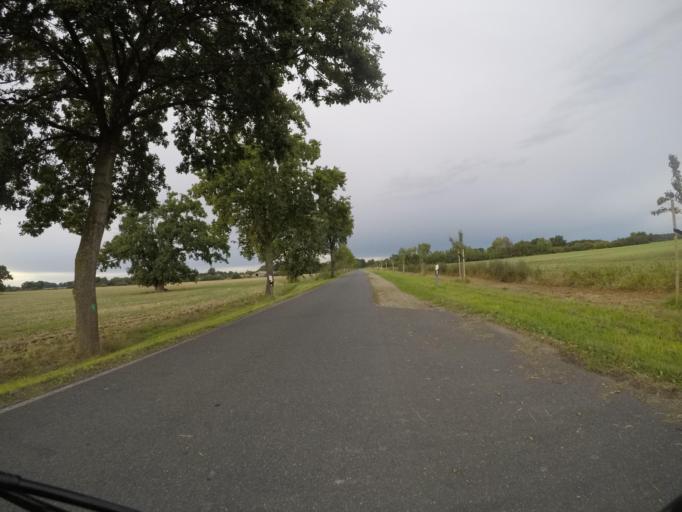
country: DE
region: Lower Saxony
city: Neu Darchau
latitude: 53.2821
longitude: 10.8733
